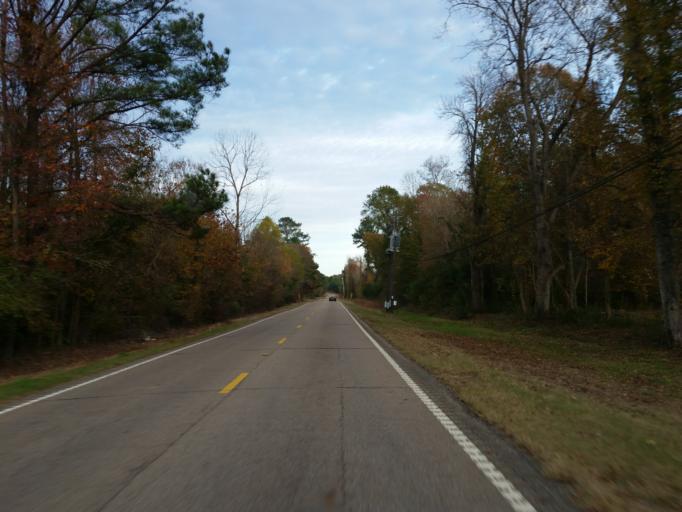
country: US
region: Mississippi
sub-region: Lauderdale County
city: Marion
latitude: 32.4120
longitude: -88.5542
